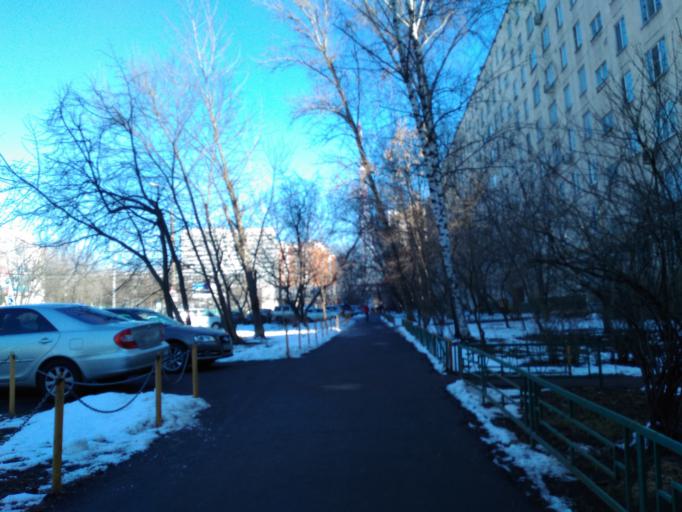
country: RU
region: Moskovskaya
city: Khoroshevo-Mnevniki
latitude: 55.7831
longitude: 37.4776
